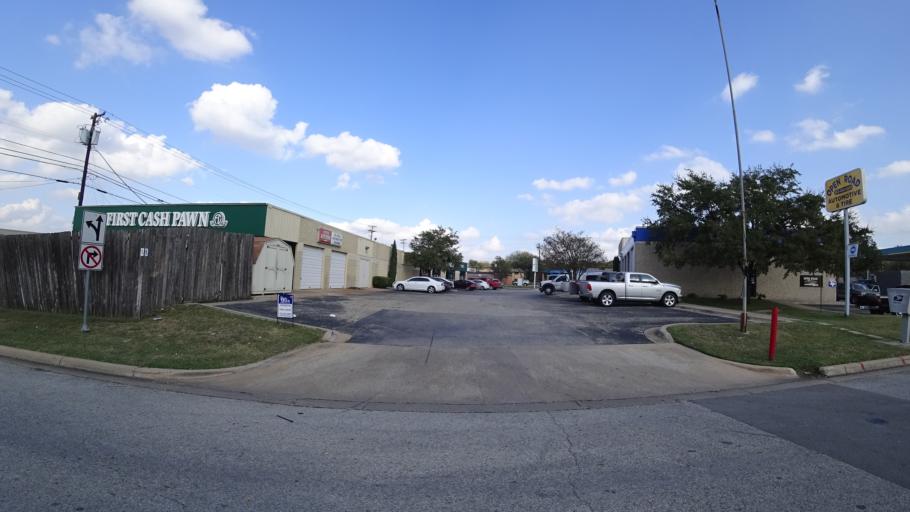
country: US
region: Texas
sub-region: Williamson County
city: Round Rock
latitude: 30.4929
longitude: -97.6767
